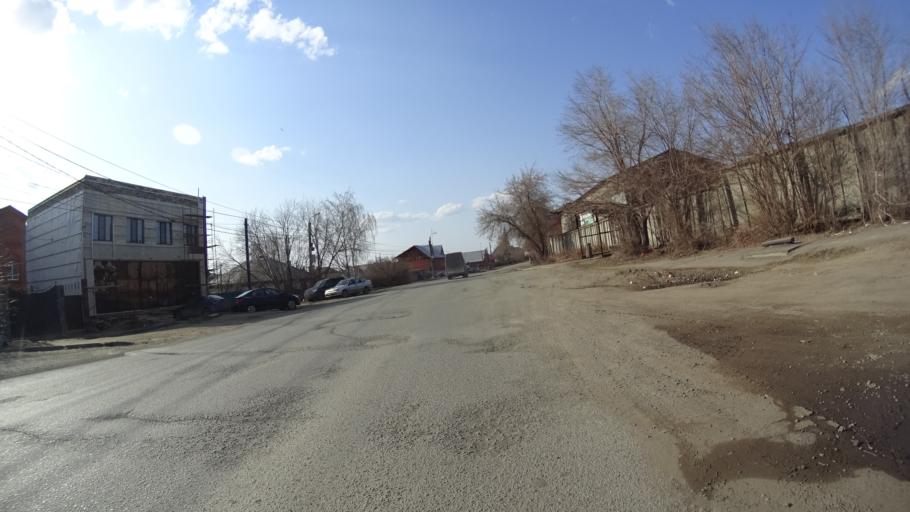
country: RU
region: Chelyabinsk
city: Novosineglazovskiy
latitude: 55.1069
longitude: 61.3363
